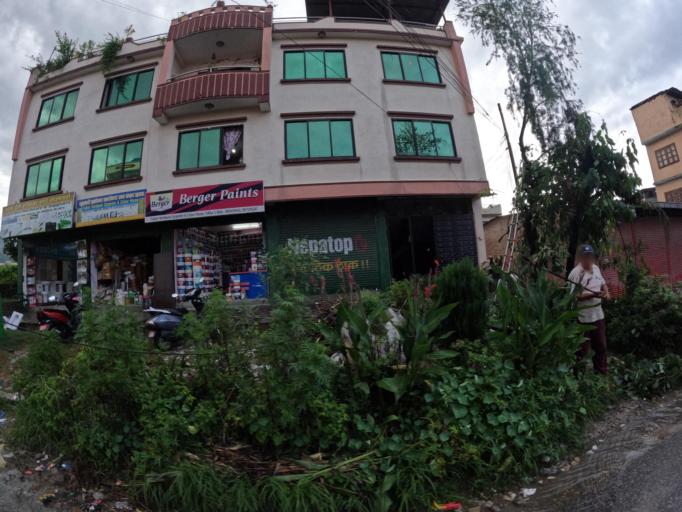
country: NP
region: Central Region
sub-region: Bagmati Zone
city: Kathmandu
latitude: 27.7633
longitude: 85.3306
